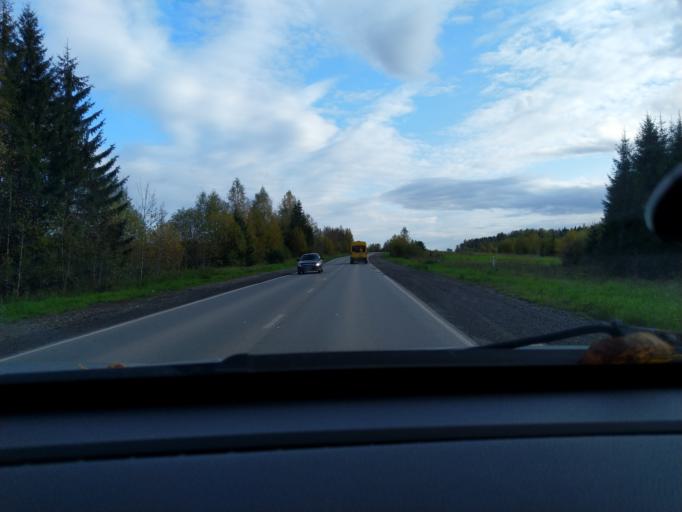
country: RU
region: Perm
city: Polazna
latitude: 58.2789
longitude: 56.4138
